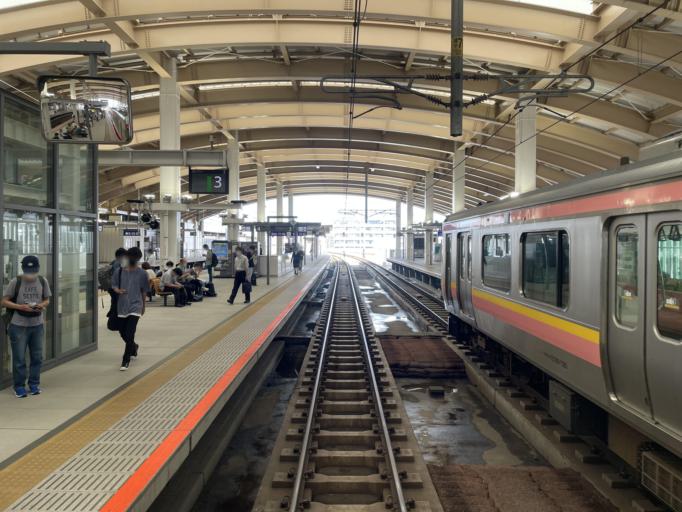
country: JP
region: Niigata
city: Niigata-shi
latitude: 37.9122
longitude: 139.0610
